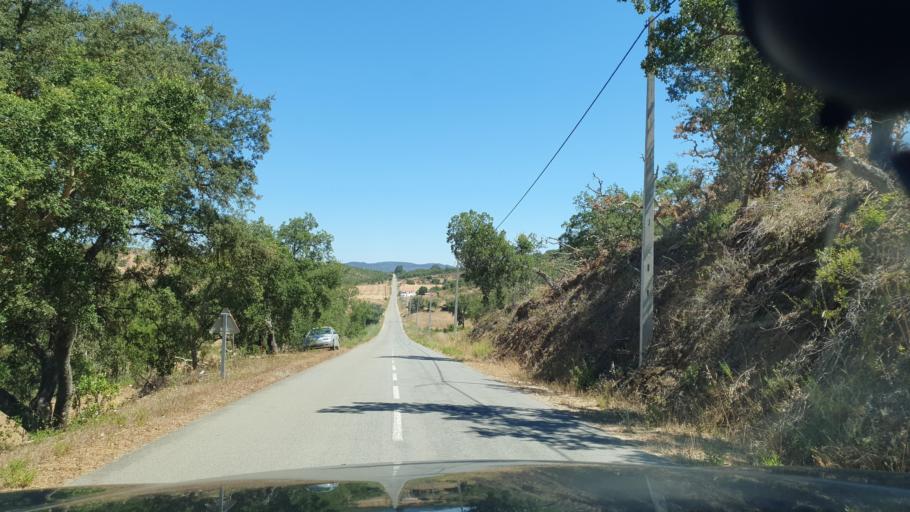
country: PT
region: Beja
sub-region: Odemira
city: Odemira
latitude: 37.5385
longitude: -8.4640
